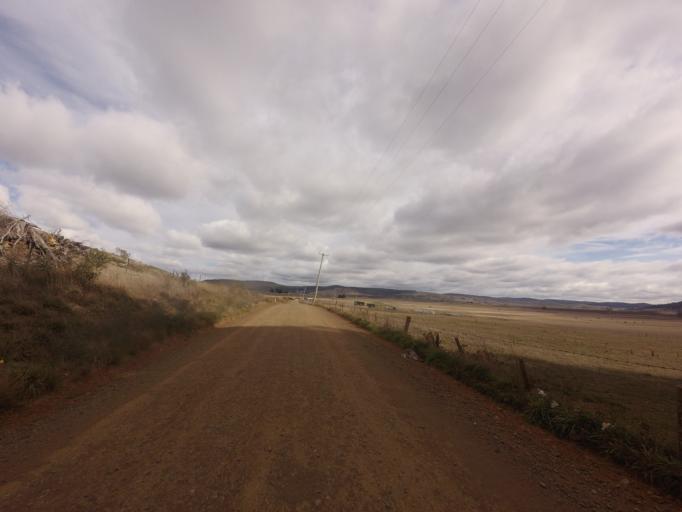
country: AU
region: Tasmania
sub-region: Brighton
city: Bridgewater
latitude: -42.4142
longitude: 147.3970
